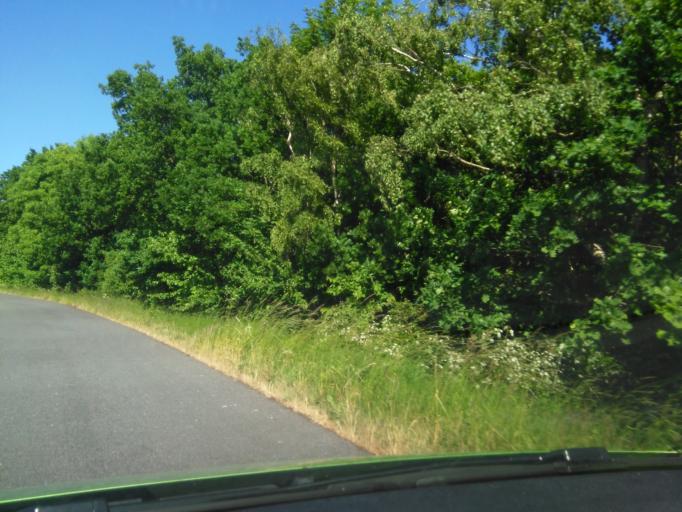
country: DK
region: Capital Region
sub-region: Bornholm Kommune
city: Nexo
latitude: 55.0660
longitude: 15.0826
